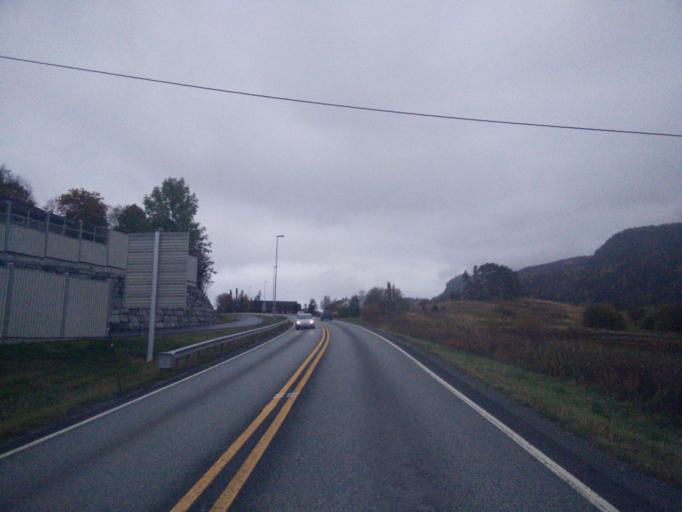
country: NO
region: Nord-Trondelag
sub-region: Stjordal
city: Stjordal
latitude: 63.4942
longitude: 10.8834
